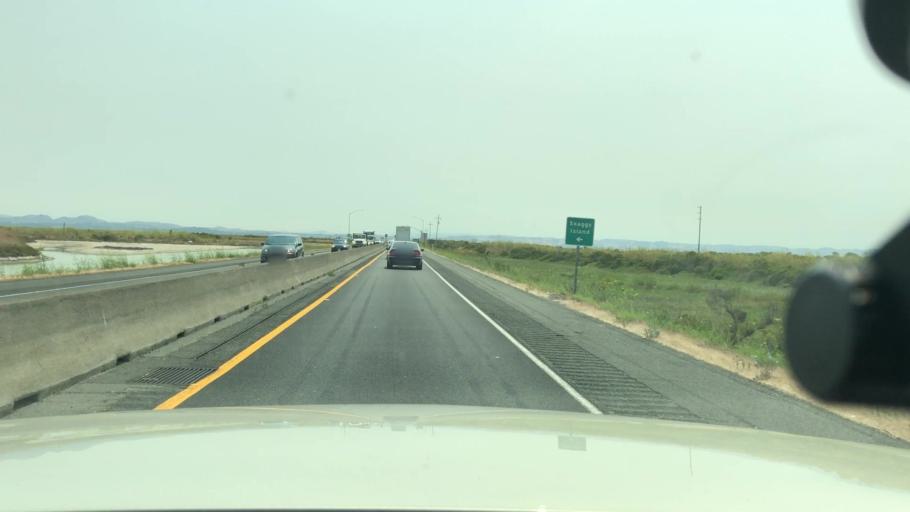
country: US
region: California
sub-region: Napa County
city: American Canyon
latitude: 38.1501
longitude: -122.3834
